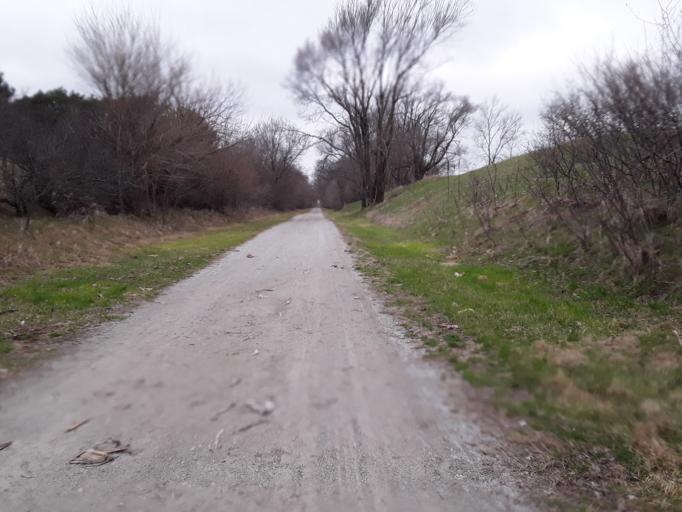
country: US
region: Nebraska
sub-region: Lancaster County
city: Lincoln
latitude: 40.8513
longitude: -96.6099
